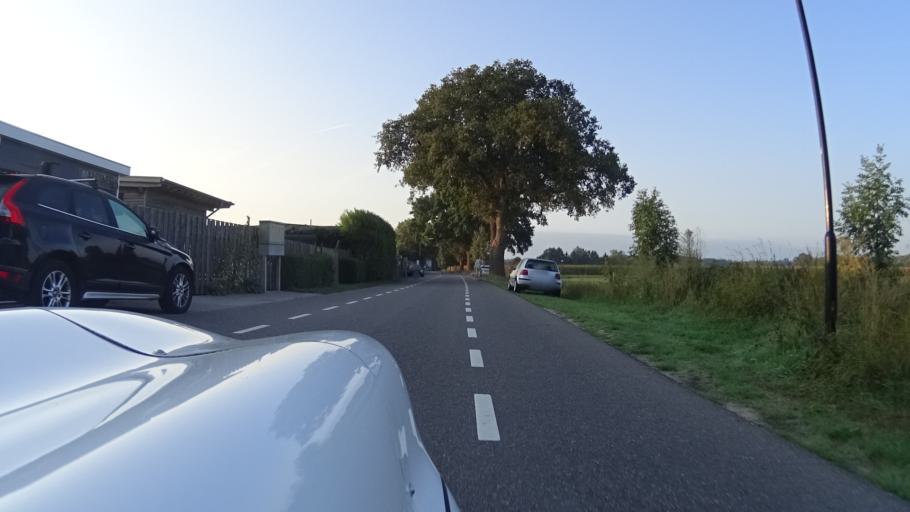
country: NL
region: Limburg
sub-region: Gemeente Venray
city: Venray
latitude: 51.5656
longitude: 6.0380
